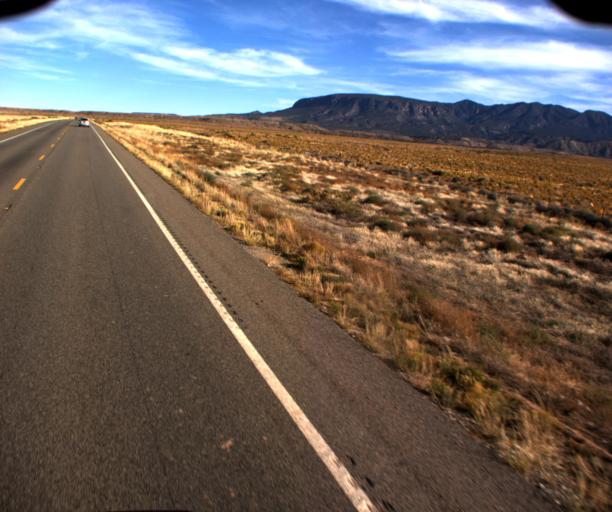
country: US
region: Arizona
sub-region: Apache County
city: Lukachukai
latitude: 36.9360
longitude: -109.2368
